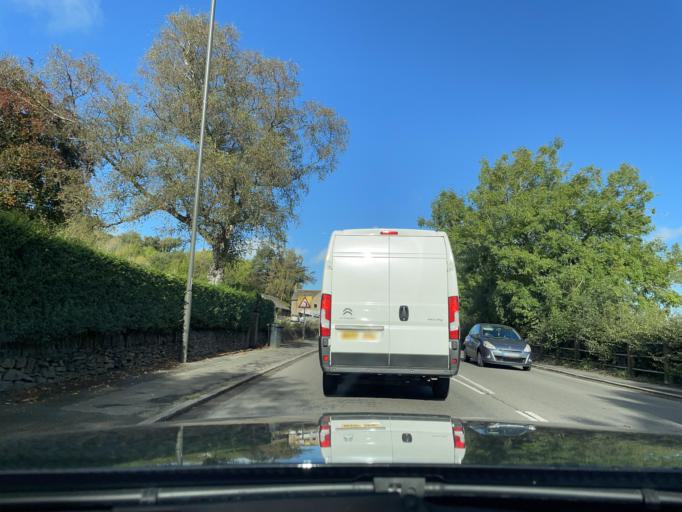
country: GB
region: England
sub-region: Derbyshire
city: New Mills
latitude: 53.3552
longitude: -1.9986
